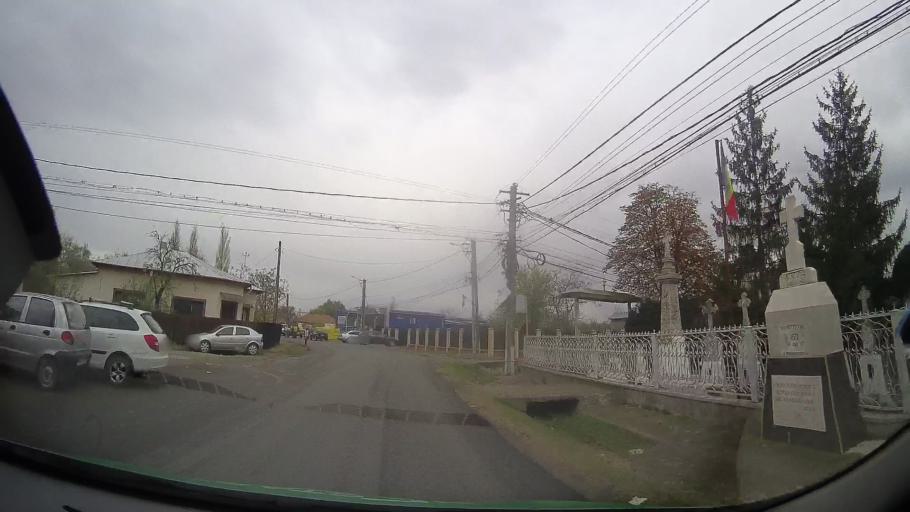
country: RO
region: Prahova
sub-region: Comuna Colceag
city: Inotesti
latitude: 44.9607
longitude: 26.3580
